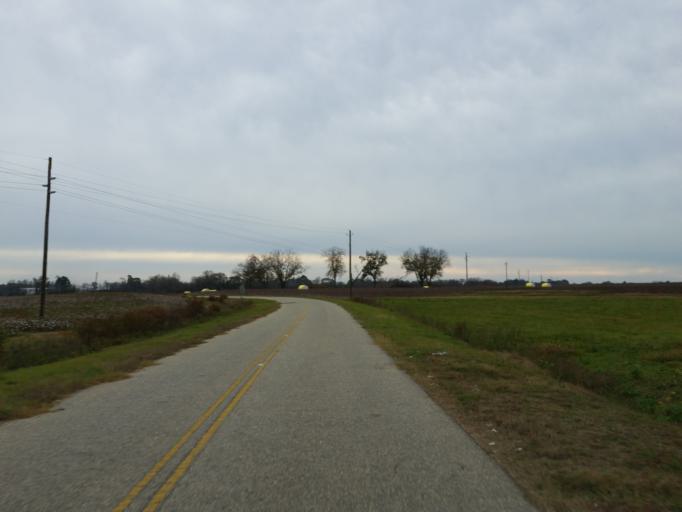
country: US
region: Georgia
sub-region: Dooly County
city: Vienna
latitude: 32.1640
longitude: -83.7761
